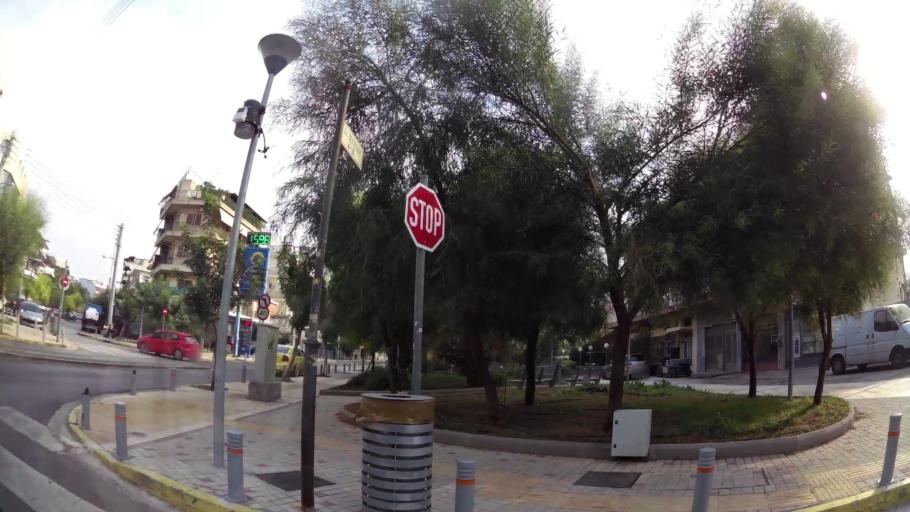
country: GR
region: Attica
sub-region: Nomarchia Athinas
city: Kallithea
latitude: 37.9565
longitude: 23.6894
